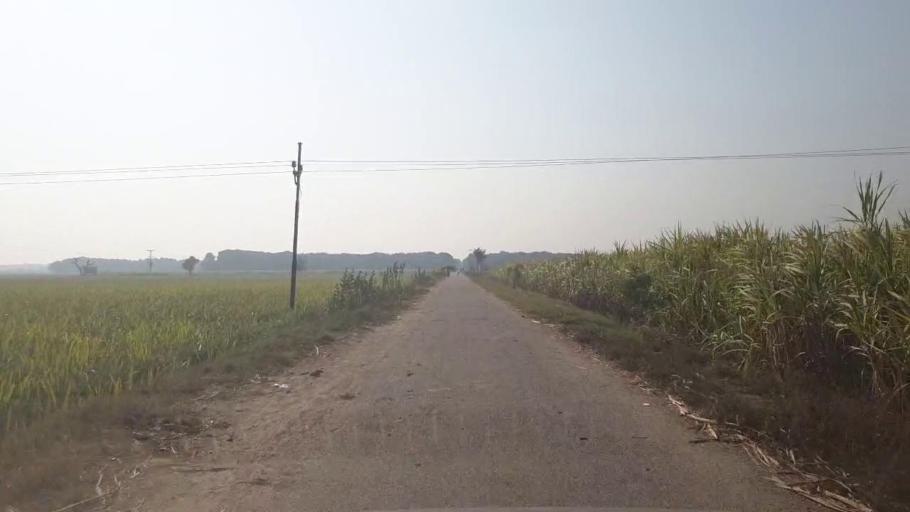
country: PK
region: Sindh
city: Tando Allahyar
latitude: 25.4754
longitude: 68.7615
